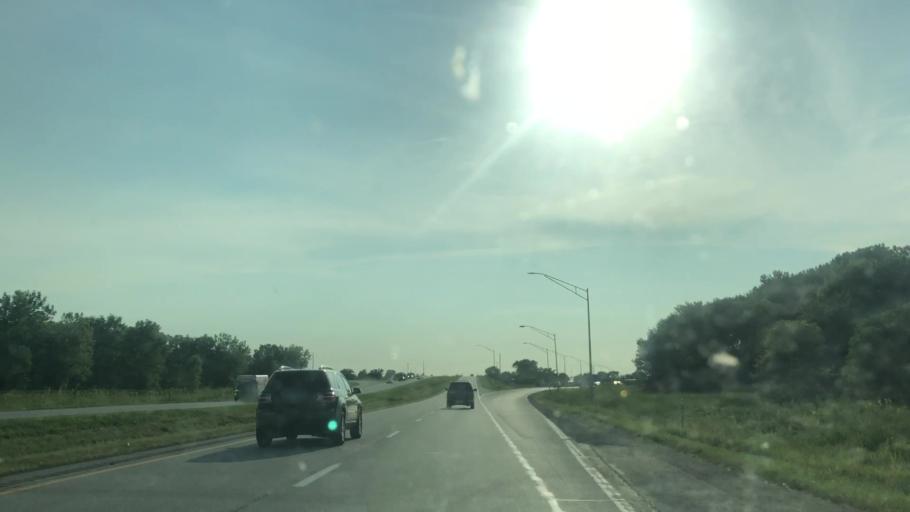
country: US
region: Iowa
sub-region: Story County
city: Ames
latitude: 42.0055
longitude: -93.6028
